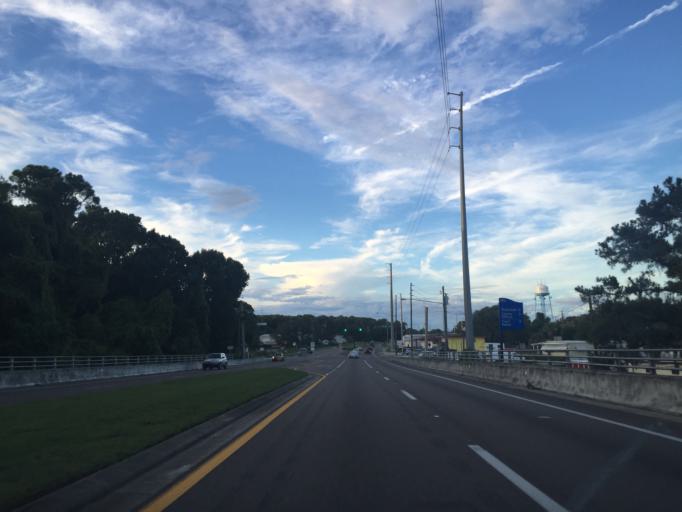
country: US
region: Florida
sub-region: Lake County
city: Tavares
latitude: 28.8013
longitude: -81.7385
